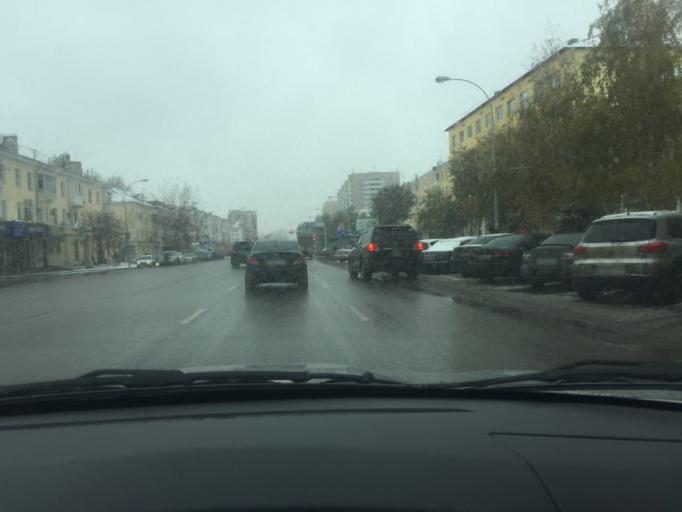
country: KZ
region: Astana Qalasy
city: Astana
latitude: 51.1683
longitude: 71.4133
